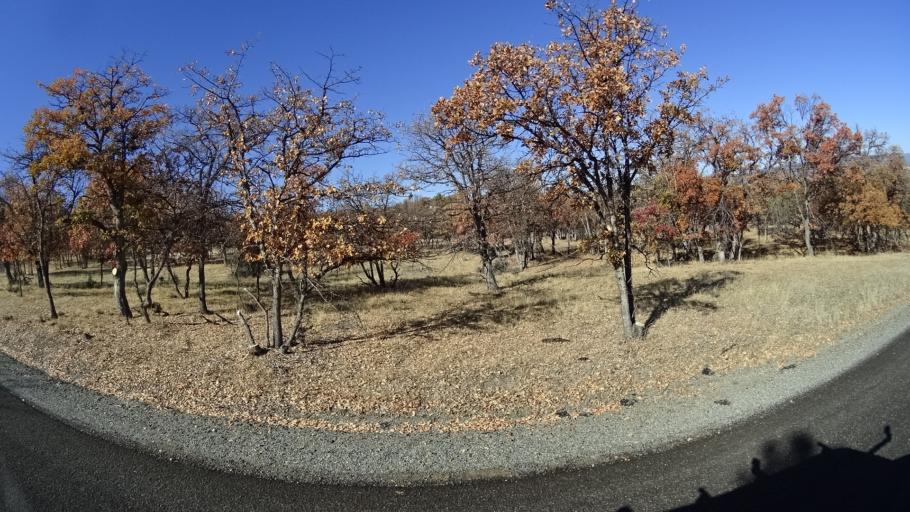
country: US
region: California
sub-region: Siskiyou County
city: Montague
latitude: 41.8780
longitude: -122.4875
